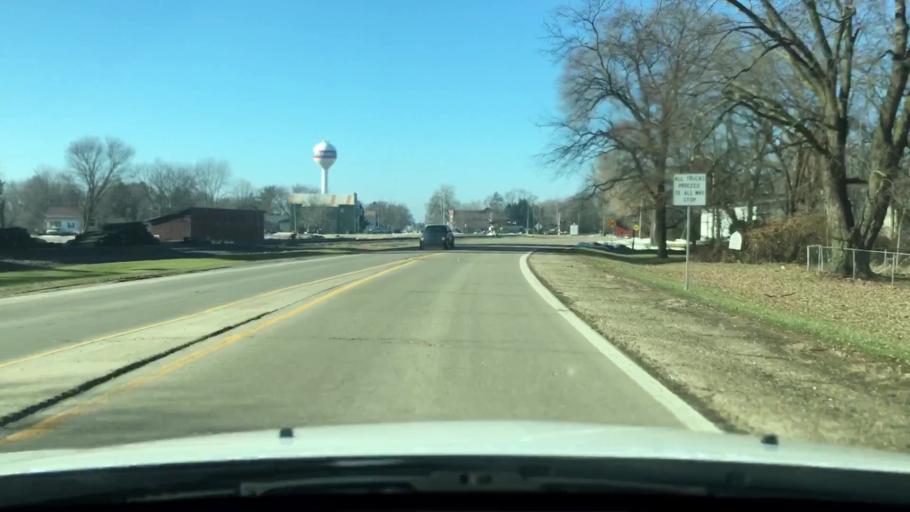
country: US
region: Illinois
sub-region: Ogle County
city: Rochelle
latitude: 41.8477
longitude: -89.0161
